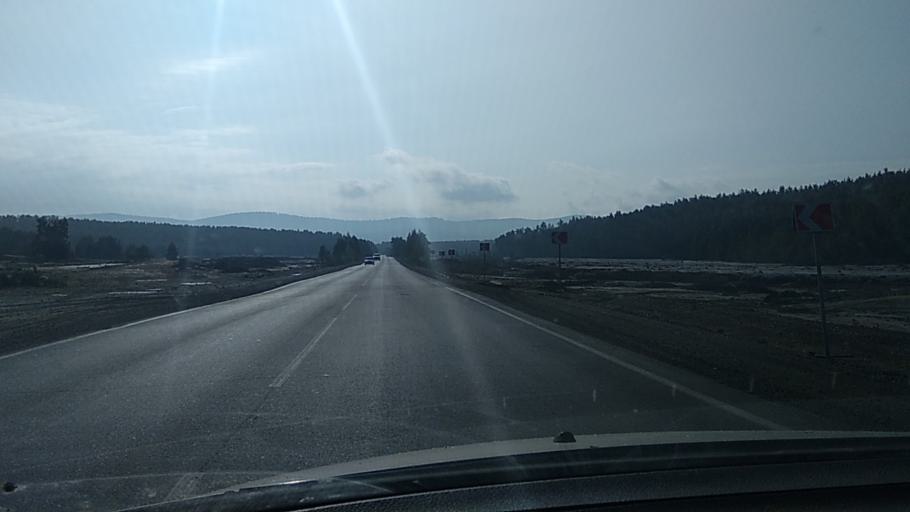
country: RU
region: Chelyabinsk
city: Karabash
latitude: 55.4399
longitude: 60.2363
